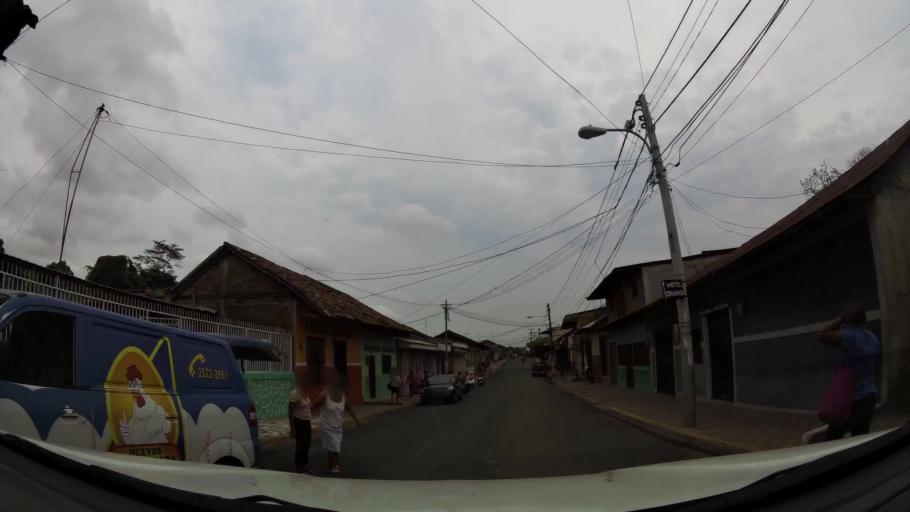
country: NI
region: Granada
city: Granada
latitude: 11.9250
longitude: -85.9641
